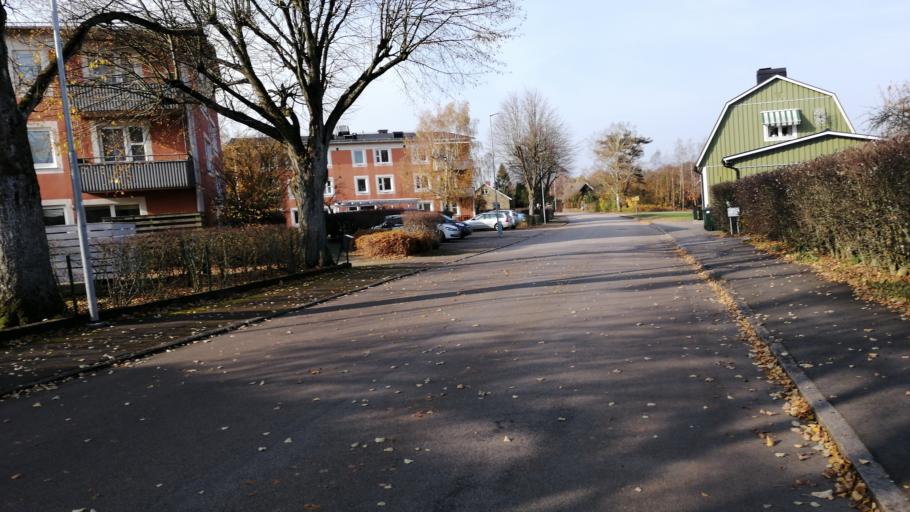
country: SE
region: Skane
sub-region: Klippans Kommun
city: Ljungbyhed
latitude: 56.0772
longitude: 13.2489
